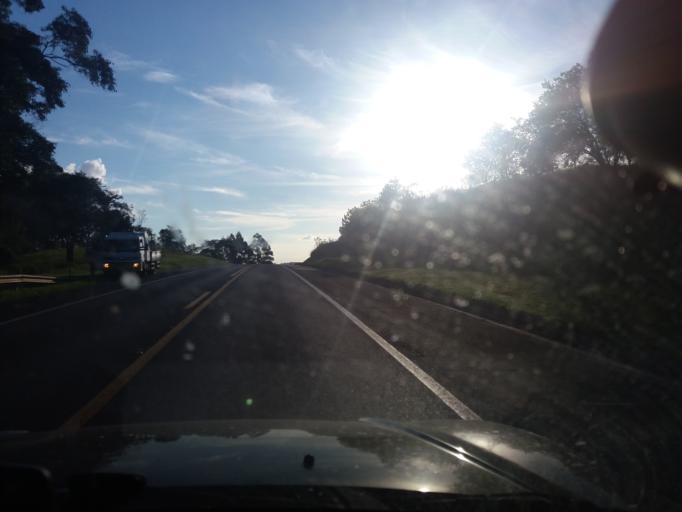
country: BR
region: Sao Paulo
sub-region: Buri
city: Buri
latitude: -23.9347
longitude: -48.6309
